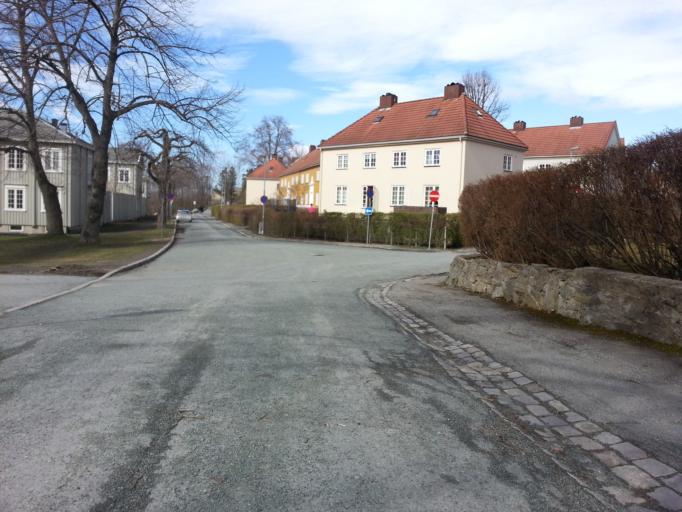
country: NO
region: Sor-Trondelag
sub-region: Trondheim
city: Trondheim
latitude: 63.4237
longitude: 10.4144
